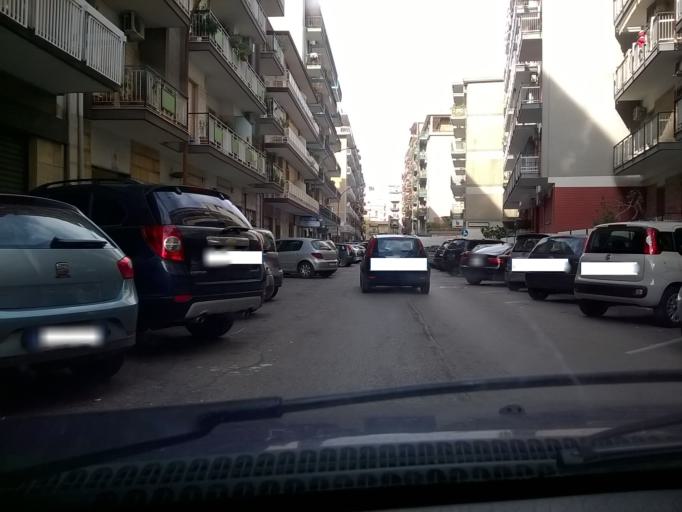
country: IT
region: Apulia
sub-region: Provincia di Taranto
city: Taranto
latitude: 40.4564
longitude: 17.2613
